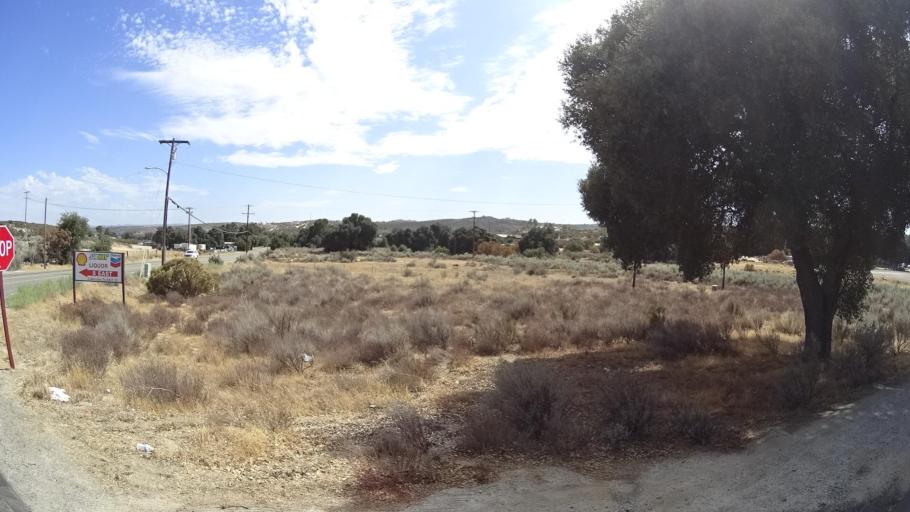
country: US
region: California
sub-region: San Diego County
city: Campo
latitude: 32.6758
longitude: -116.2912
